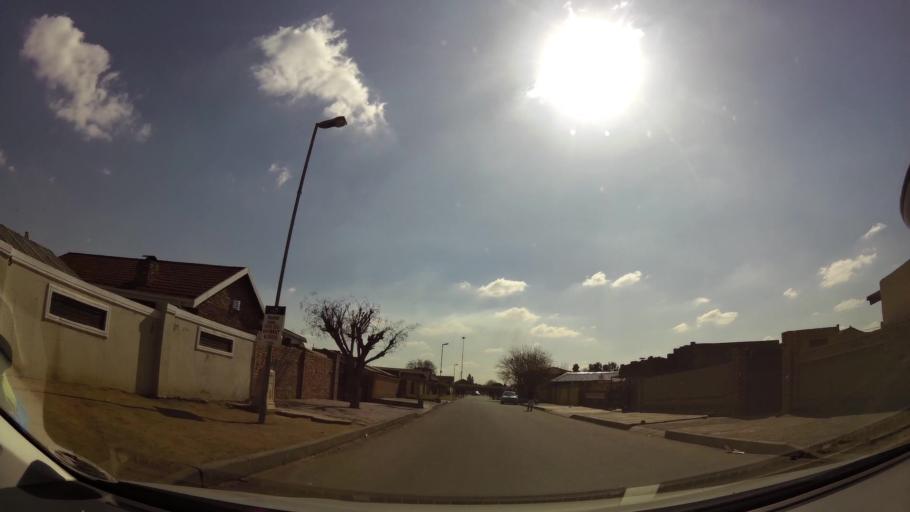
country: ZA
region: Gauteng
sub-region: City of Johannesburg Metropolitan Municipality
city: Soweto
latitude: -26.2521
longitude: 27.8877
